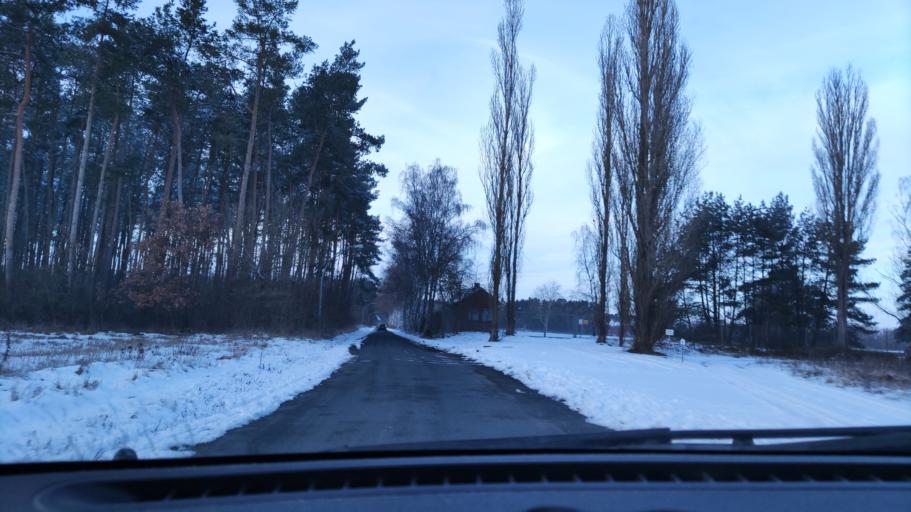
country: DE
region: Lower Saxony
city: Tosterglope
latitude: 53.2668
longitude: 10.8020
